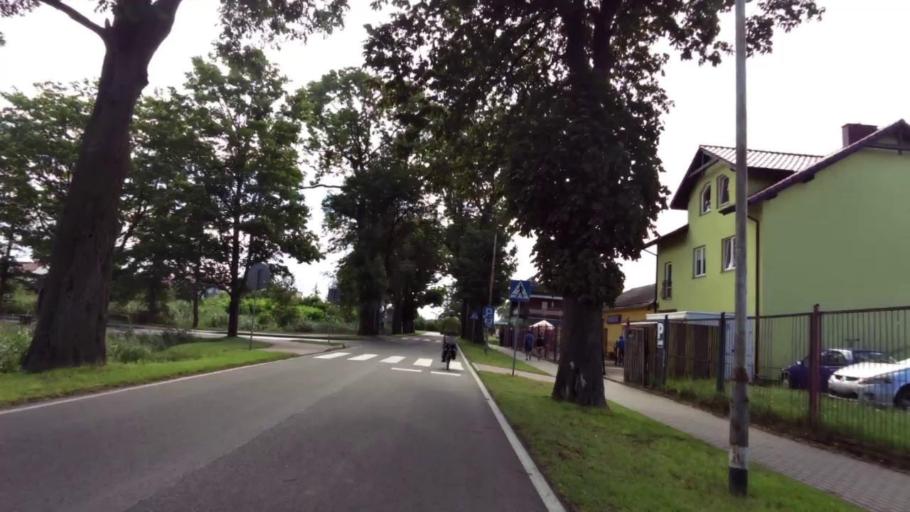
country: PL
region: West Pomeranian Voivodeship
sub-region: Powiat slawienski
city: Darlowo
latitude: 54.4380
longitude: 16.3873
